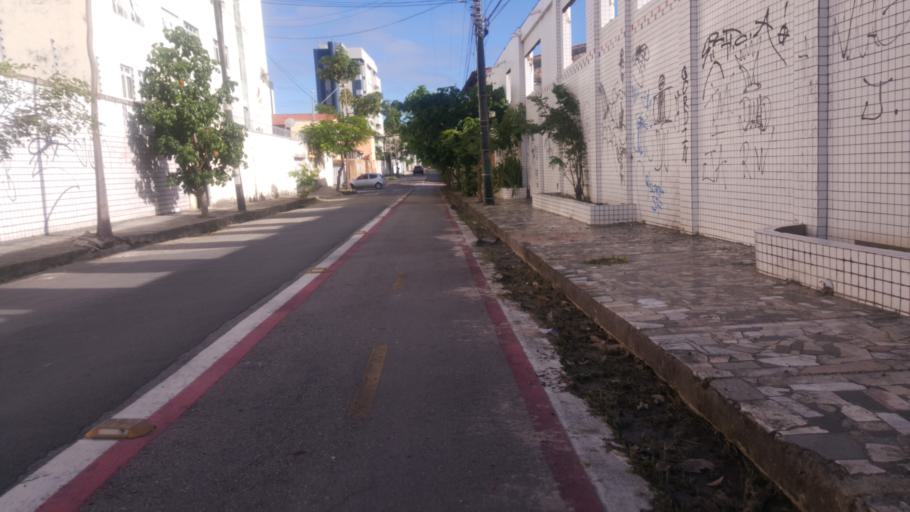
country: BR
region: Ceara
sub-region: Fortaleza
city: Fortaleza
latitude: -3.7465
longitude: -38.5387
